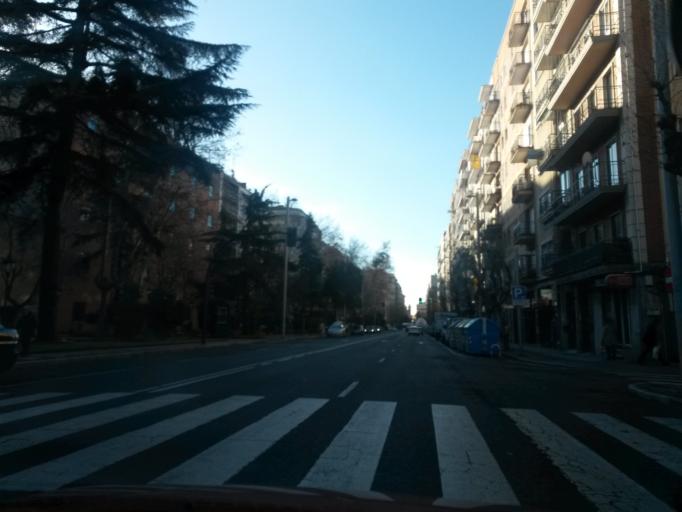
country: ES
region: Castille and Leon
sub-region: Provincia de Salamanca
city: Salamanca
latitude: 40.9745
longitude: -5.6629
